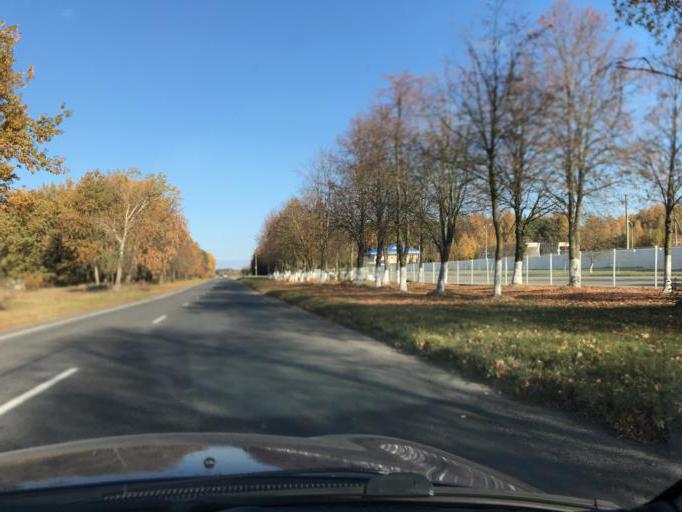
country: BY
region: Grodnenskaya
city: Lida
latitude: 53.9427
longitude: 25.2457
